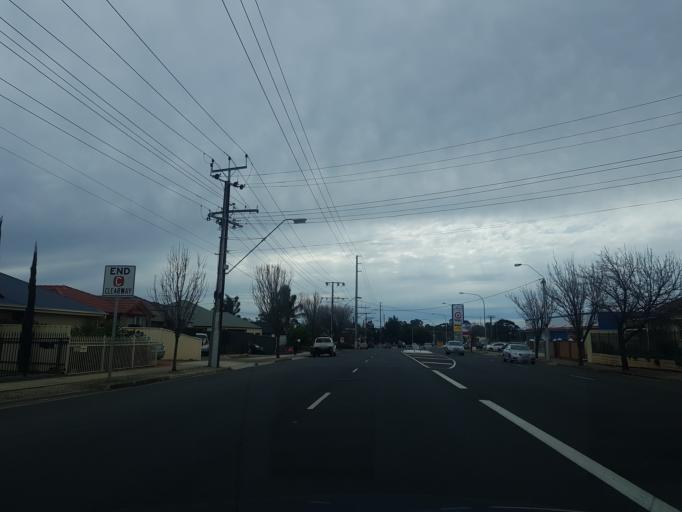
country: AU
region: South Australia
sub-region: Campbelltown
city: Campbelltown
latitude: -34.8803
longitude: 138.6736
